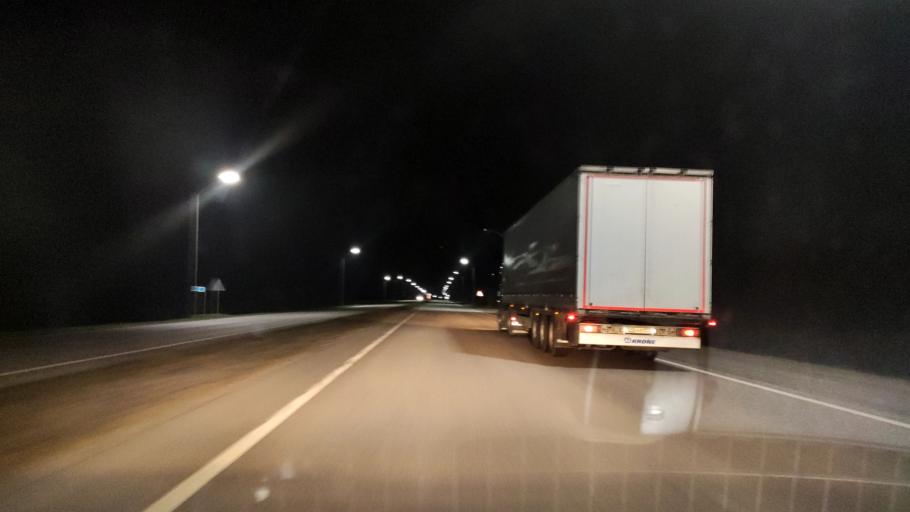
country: RU
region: Belgorod
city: Staryy Oskol
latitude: 51.3727
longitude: 37.8473
